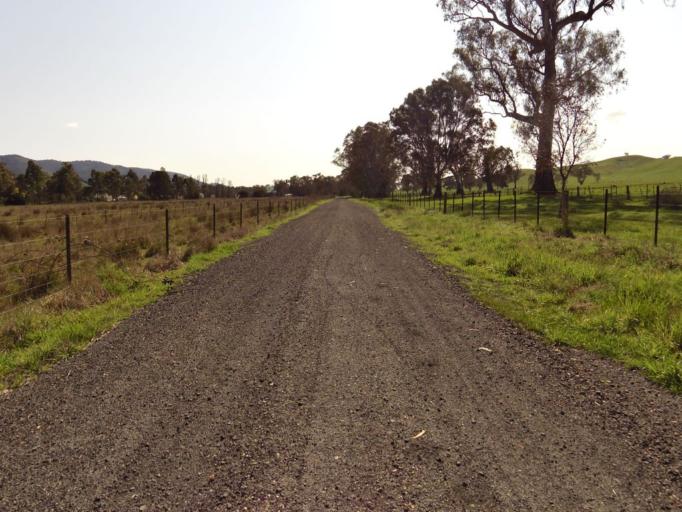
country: AU
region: Victoria
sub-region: Murrindindi
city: Alexandra
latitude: -37.1470
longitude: 145.5878
